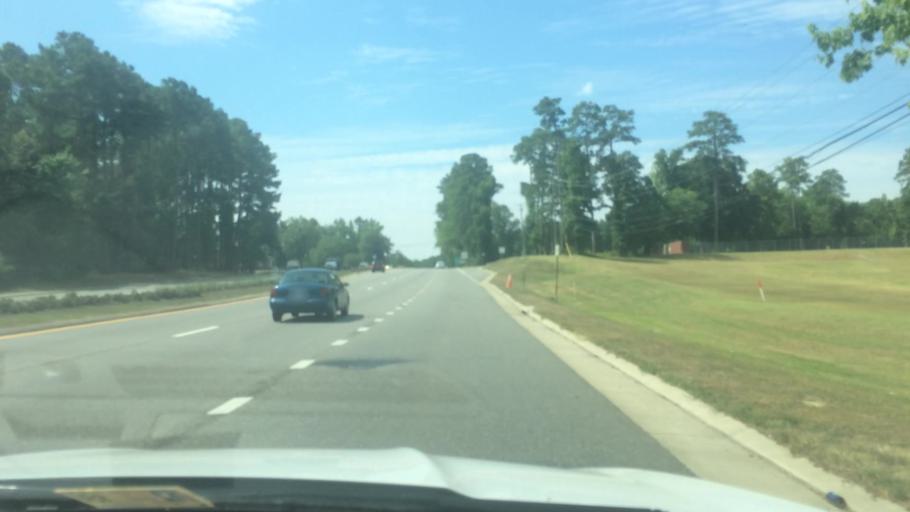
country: US
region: Virginia
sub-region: City of Poquoson
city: Poquoson
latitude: 37.1364
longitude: -76.4575
